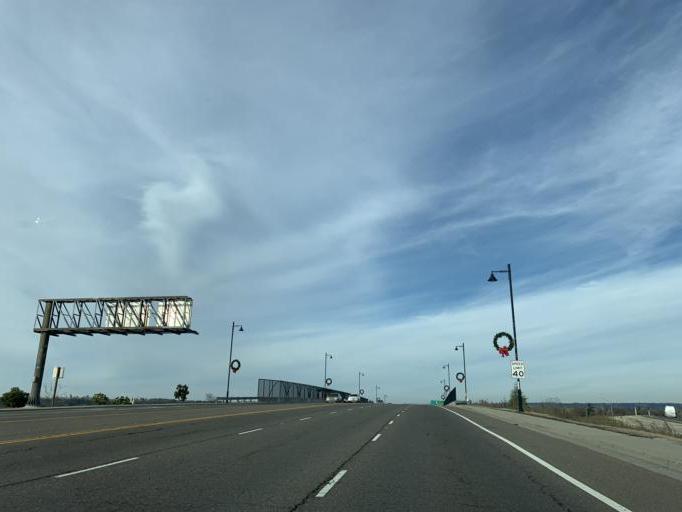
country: US
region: California
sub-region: Placer County
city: Loomis
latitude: 38.8016
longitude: -121.2054
